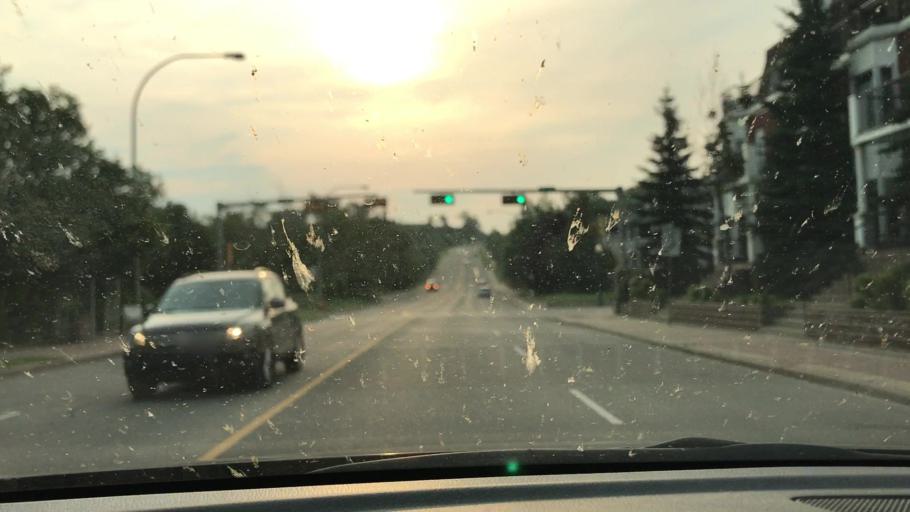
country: CA
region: Alberta
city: Edmonton
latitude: 53.5384
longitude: -113.4695
